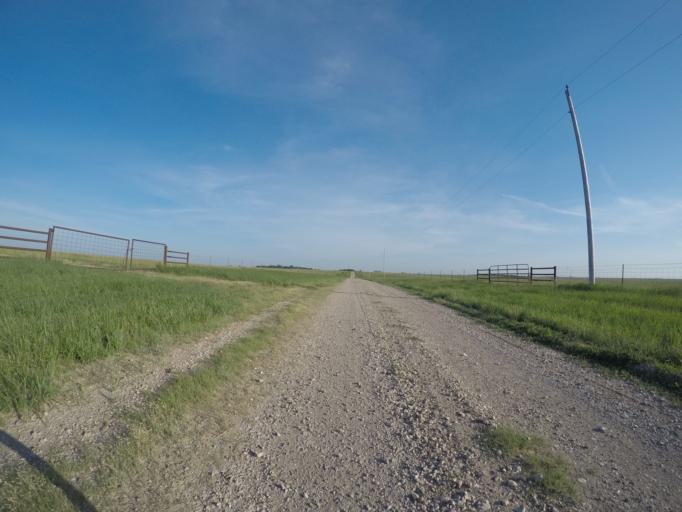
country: US
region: Kansas
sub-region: Wabaunsee County
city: Alma
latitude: 38.9955
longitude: -96.4921
